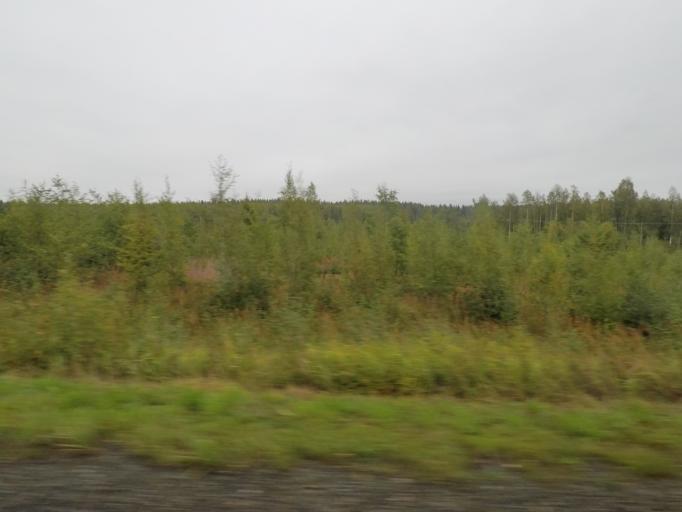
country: FI
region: Northern Savo
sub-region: Varkaus
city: Leppaevirta
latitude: 62.5400
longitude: 27.6348
